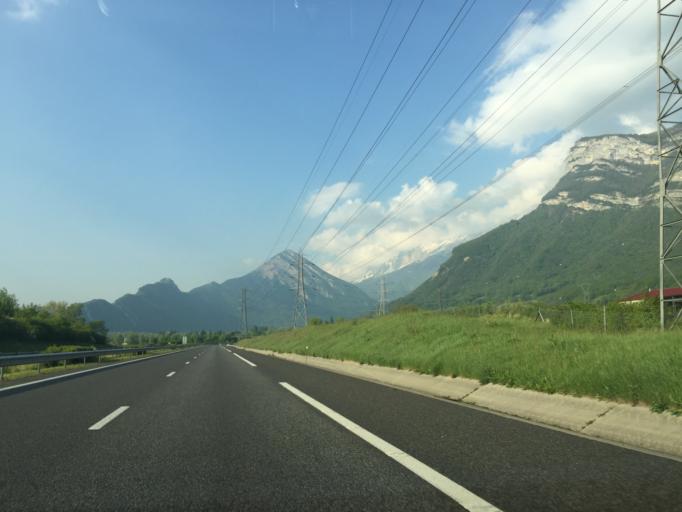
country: FR
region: Rhone-Alpes
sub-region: Departement de l'Isere
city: Allieres-et-Risset
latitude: 45.1029
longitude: 5.6762
